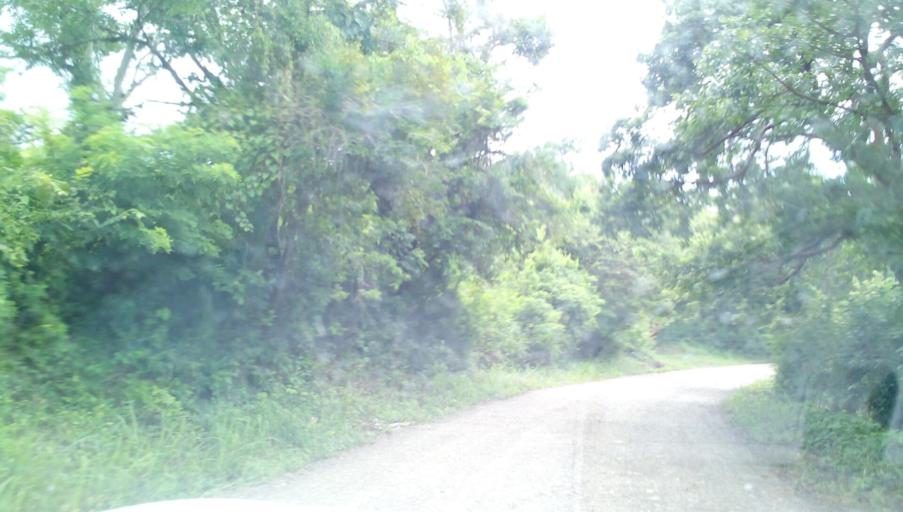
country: MX
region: Veracruz
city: Tepetzintla
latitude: 21.1384
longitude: -97.8513
